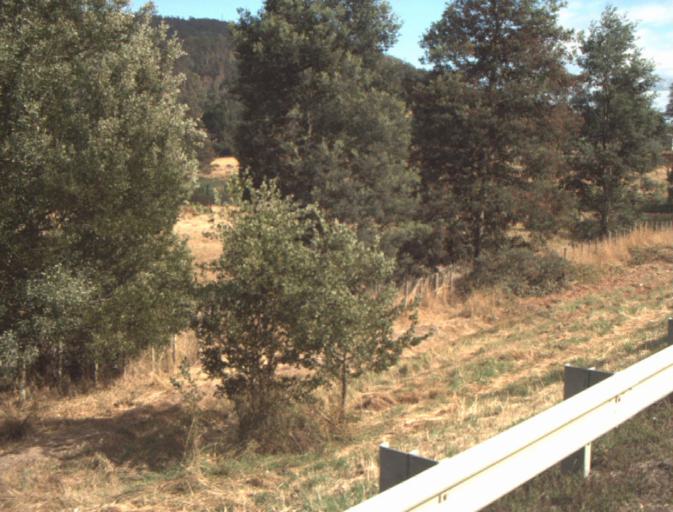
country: AU
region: Tasmania
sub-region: Launceston
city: Mayfield
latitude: -41.2894
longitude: 147.2173
